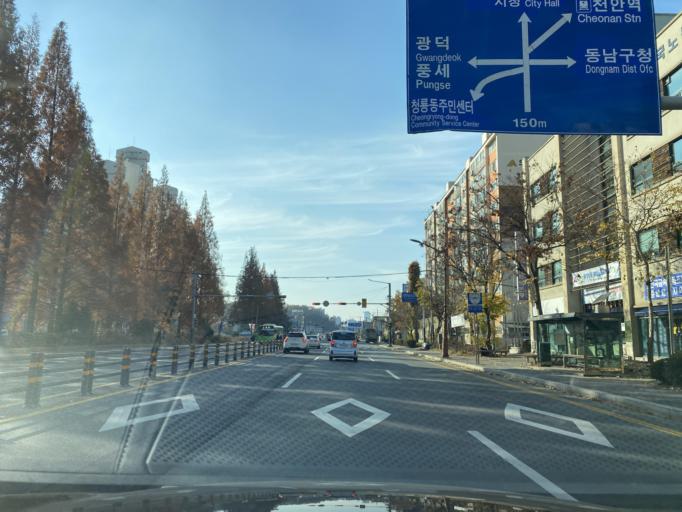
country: KR
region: Chungcheongnam-do
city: Cheonan
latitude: 36.7986
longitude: 127.1565
